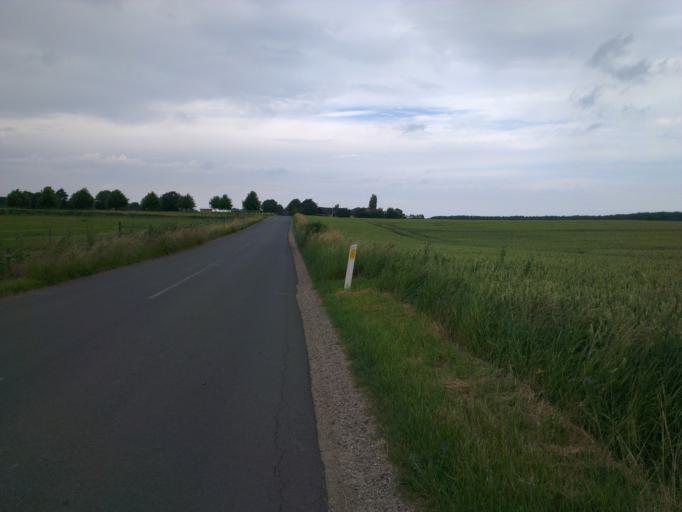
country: DK
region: Capital Region
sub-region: Frederikssund Kommune
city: Skibby
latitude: 55.7658
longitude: 11.9494
